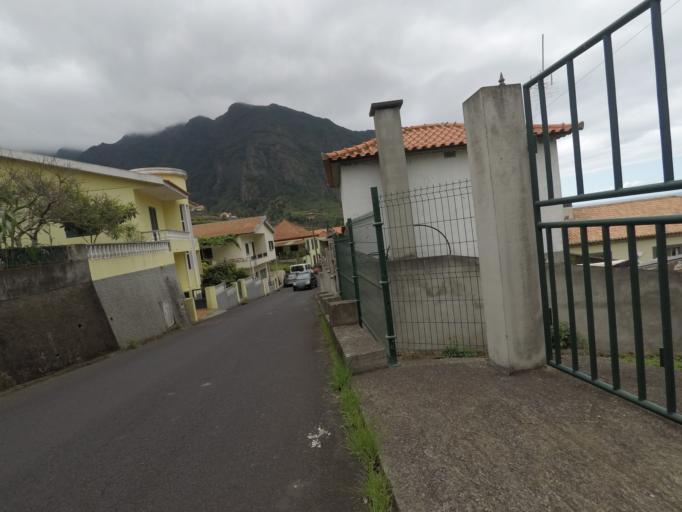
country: PT
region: Madeira
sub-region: Sao Vicente
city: Sao Vicente
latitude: 32.7906
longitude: -17.0382
